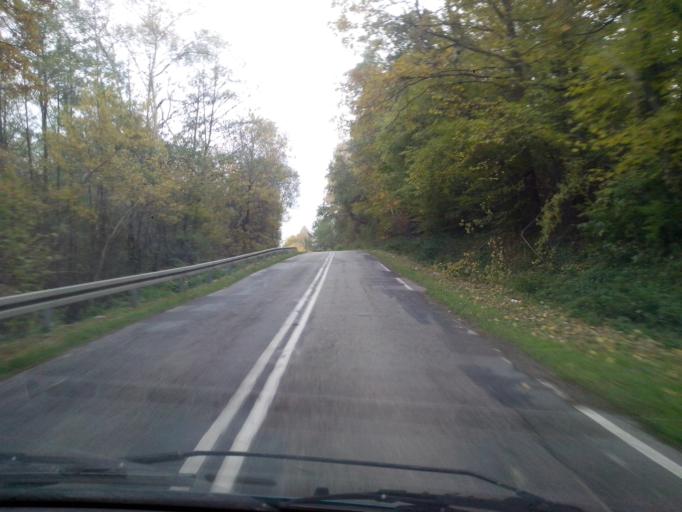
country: PL
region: Subcarpathian Voivodeship
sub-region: Powiat strzyzowski
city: Wisniowa
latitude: 49.8764
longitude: 21.6488
